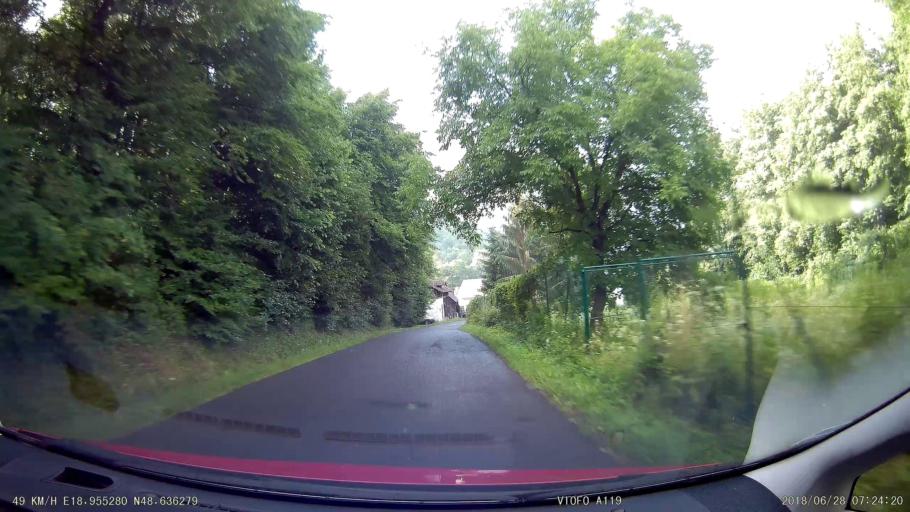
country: SK
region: Banskobystricky
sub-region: Okres Ziar nad Hronom
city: Kremnica
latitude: 48.6360
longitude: 18.9554
